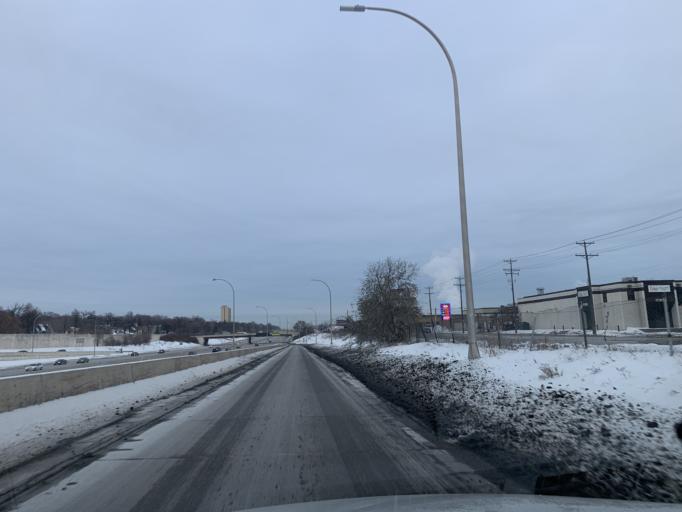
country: US
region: Minnesota
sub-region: Hennepin County
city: Minneapolis
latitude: 45.0022
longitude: -93.2821
